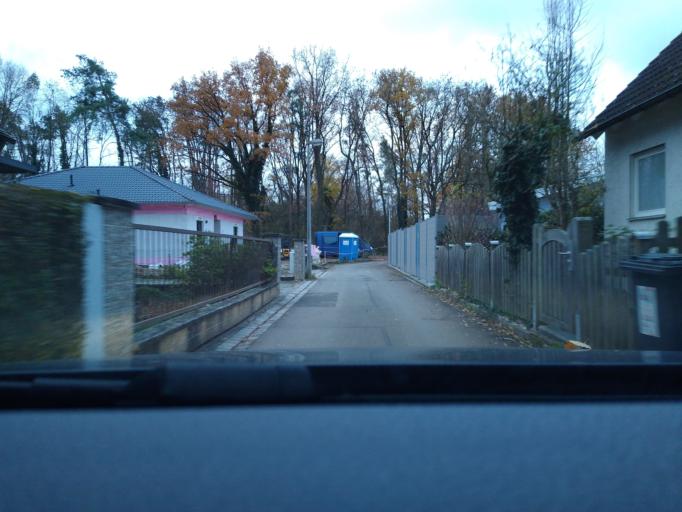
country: DE
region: Bavaria
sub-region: Regierungsbezirk Mittelfranken
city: Wetzendorf
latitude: 49.5096
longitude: 11.0581
